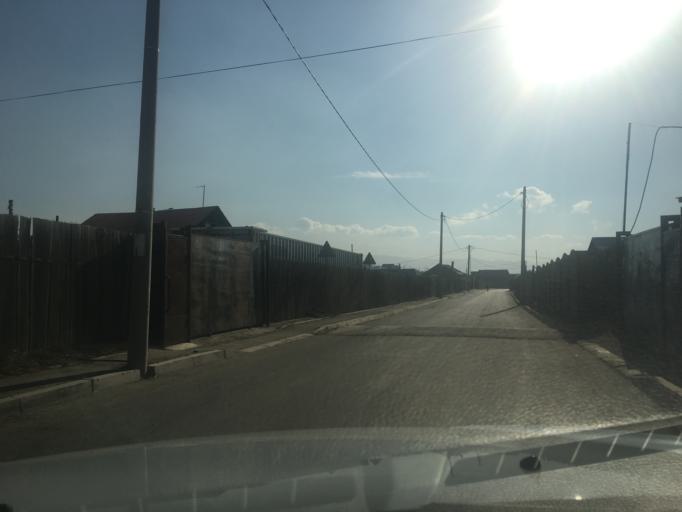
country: MN
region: Ulaanbaatar
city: Ulaanbaatar
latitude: 47.9668
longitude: 106.8270
